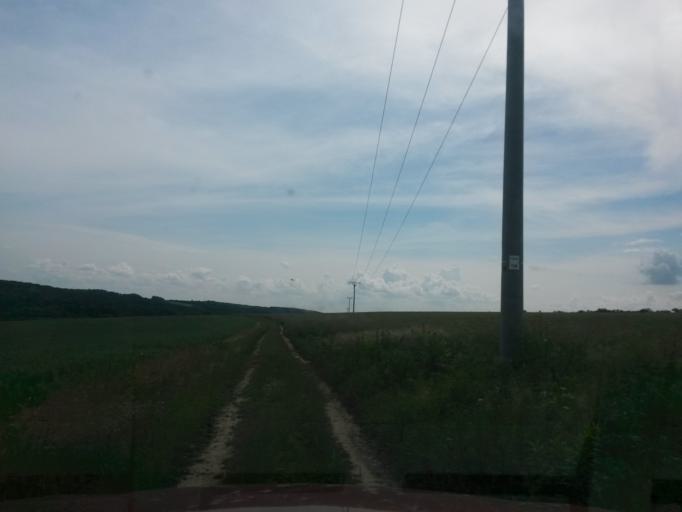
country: SK
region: Kosicky
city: Moldava nad Bodvou
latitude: 48.6586
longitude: 21.1102
